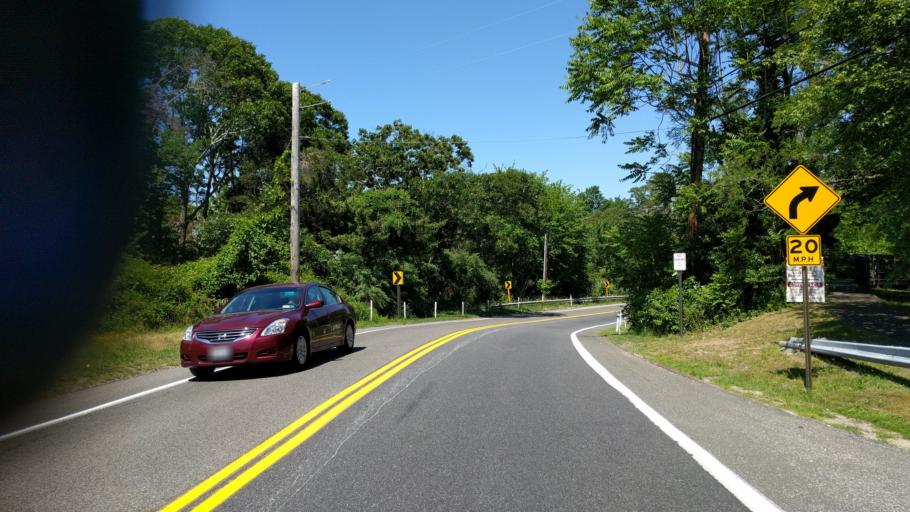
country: US
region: New York
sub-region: Suffolk County
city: Noyack
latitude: 40.9930
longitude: -72.3503
